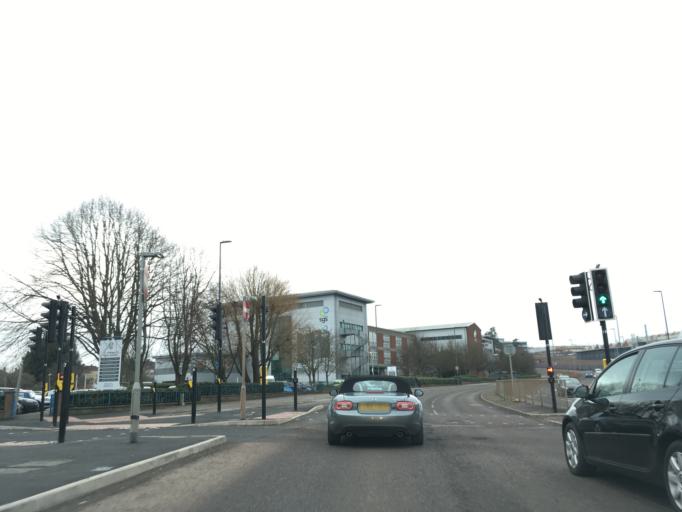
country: GB
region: England
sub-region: South Gloucestershire
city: Stoke Gifford
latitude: 51.5151
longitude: -2.5722
